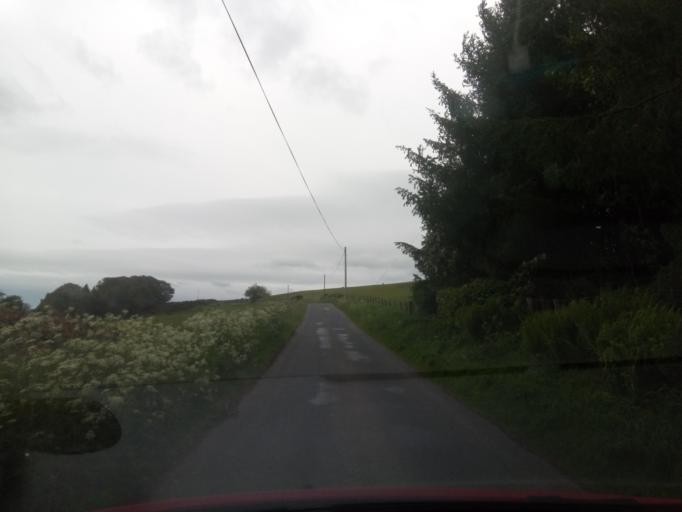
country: GB
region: Scotland
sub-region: The Scottish Borders
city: Selkirk
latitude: 55.5580
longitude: -2.7978
